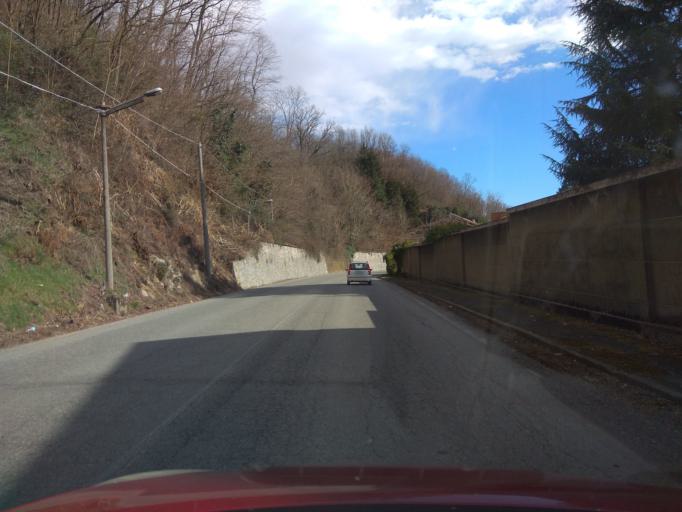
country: IT
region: Piedmont
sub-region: Provincia di Biella
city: Fontanella-Ozino
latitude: 45.6166
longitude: 8.1621
